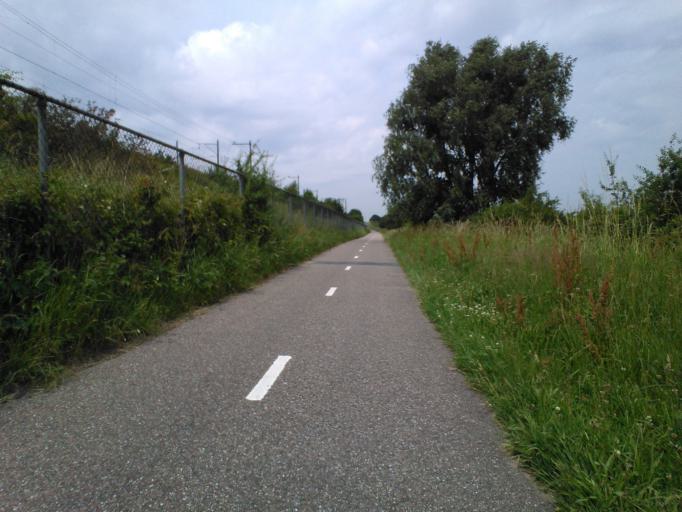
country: NL
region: North Holland
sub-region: Gemeente Amsterdam
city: Driemond
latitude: 52.3214
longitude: 5.0259
